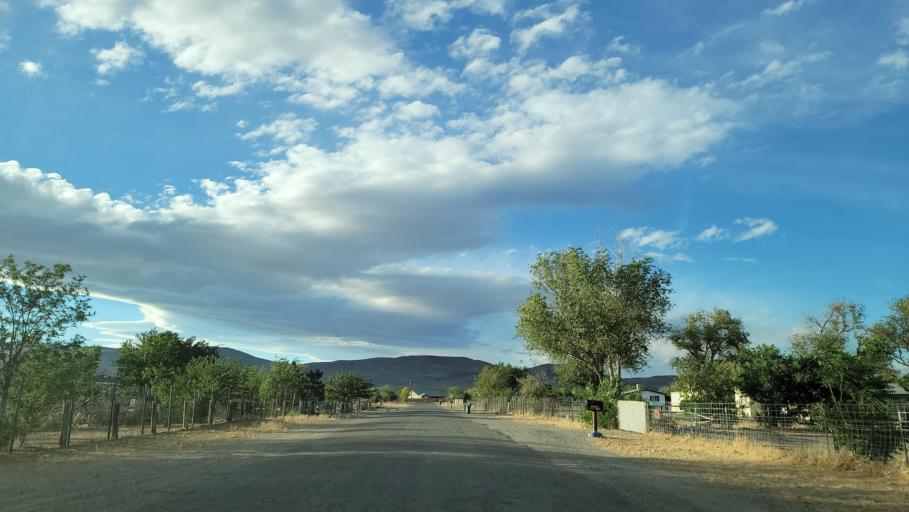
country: US
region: Nevada
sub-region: Lyon County
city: Silver Springs
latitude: 39.3977
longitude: -119.2374
